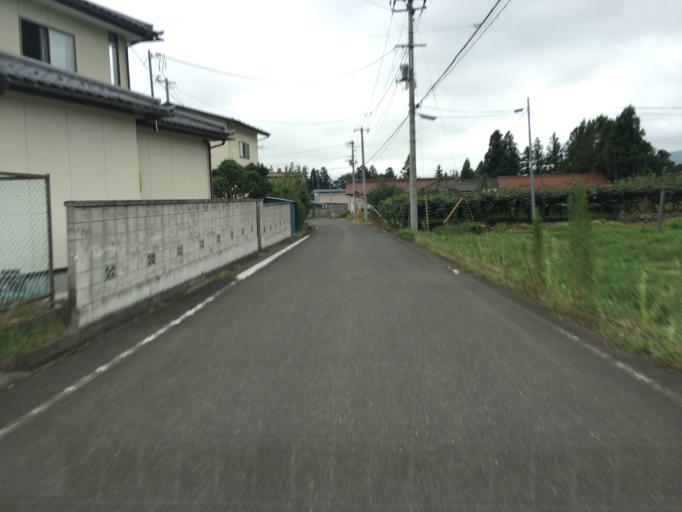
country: JP
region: Fukushima
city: Fukushima-shi
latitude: 37.7802
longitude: 140.3831
